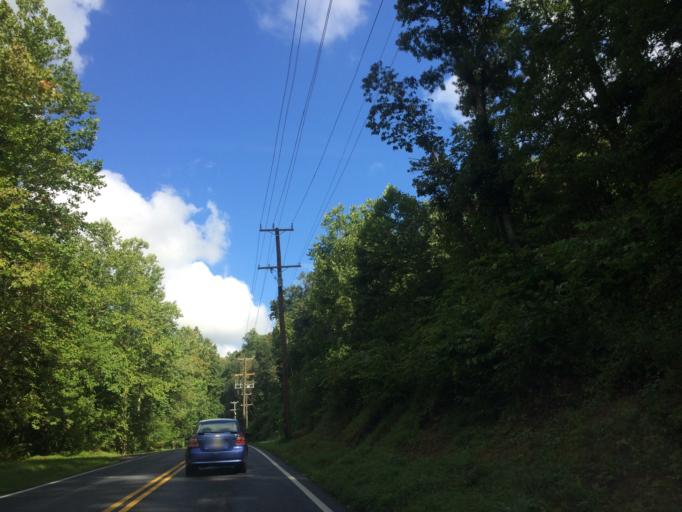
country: US
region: Maryland
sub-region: Carroll County
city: Eldersburg
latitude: 39.3642
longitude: -76.9077
